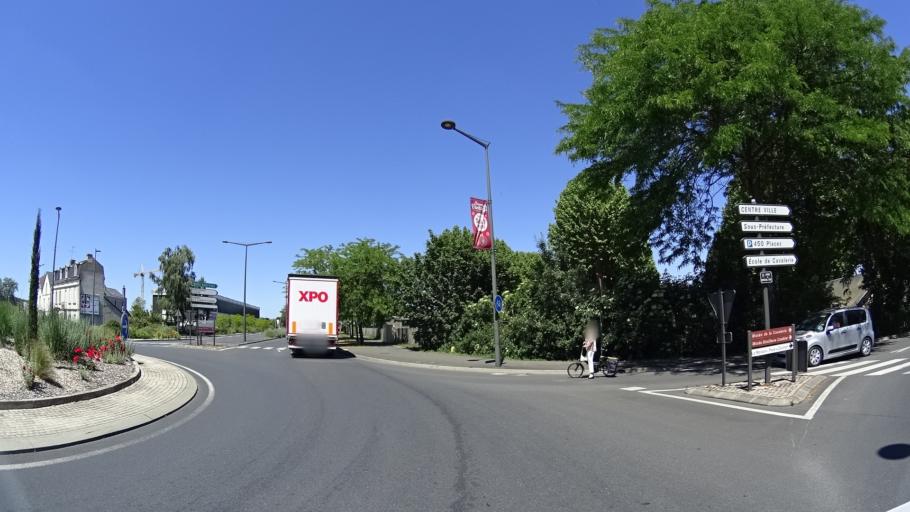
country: FR
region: Pays de la Loire
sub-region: Departement de Maine-et-Loire
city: Saumur
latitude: 47.2627
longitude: -0.0901
